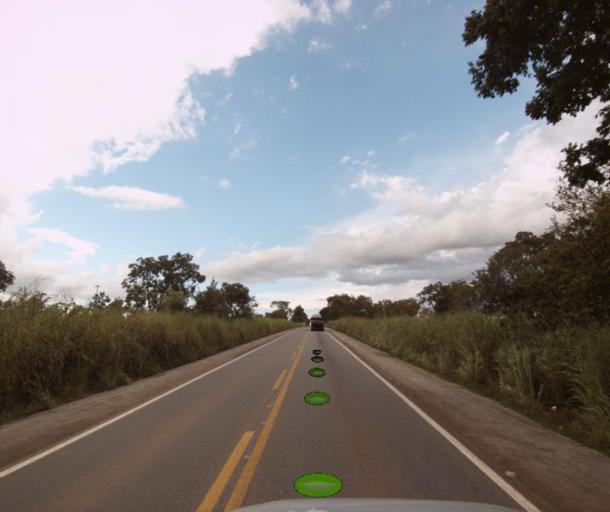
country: BR
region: Goias
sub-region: Porangatu
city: Porangatu
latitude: -13.3782
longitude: -49.1270
